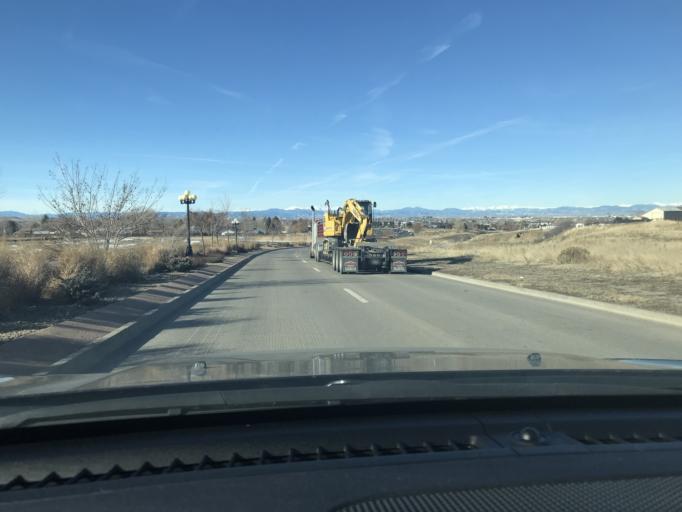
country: US
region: Colorado
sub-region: Douglas County
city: Parker
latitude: 39.5364
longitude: -104.7592
